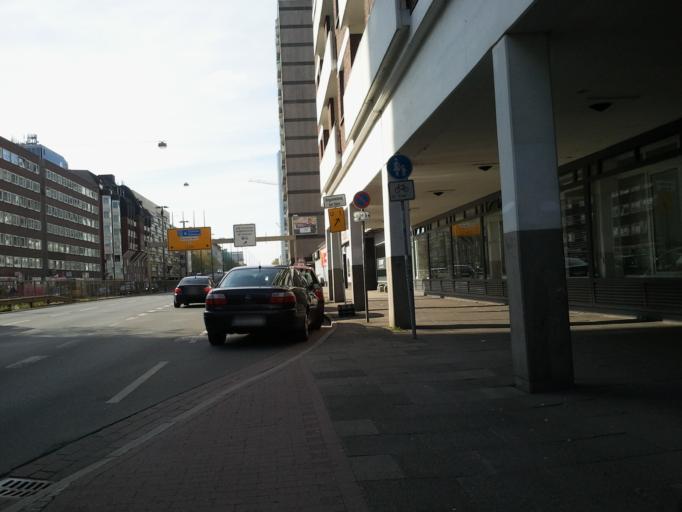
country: DE
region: Bremen
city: Bremen
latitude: 53.0789
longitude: 8.8168
